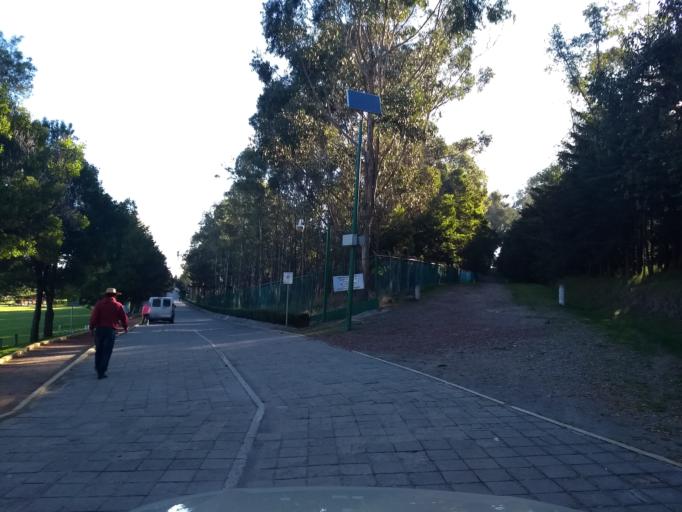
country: MX
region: Mexico
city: San Marcos Yachihuacaltepec
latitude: 19.3085
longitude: -99.6872
